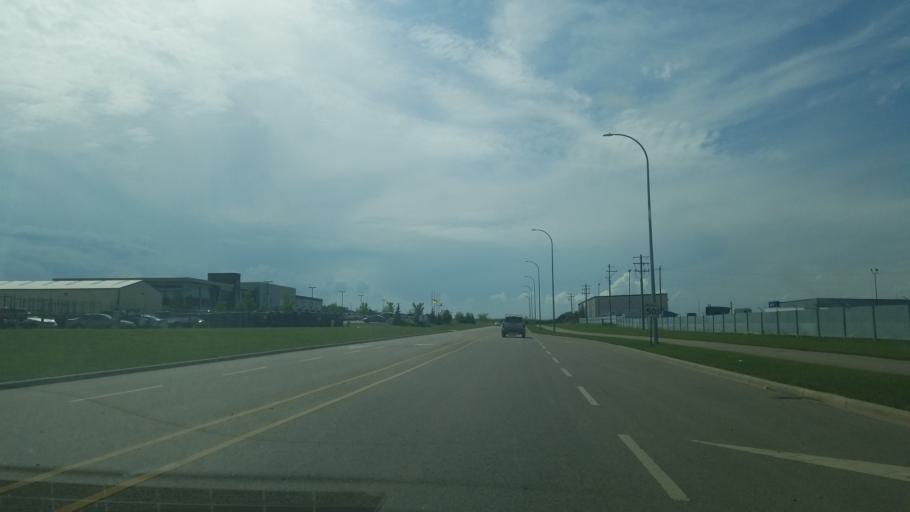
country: CA
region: Saskatchewan
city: Lloydminster
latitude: 53.2867
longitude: -110.0371
